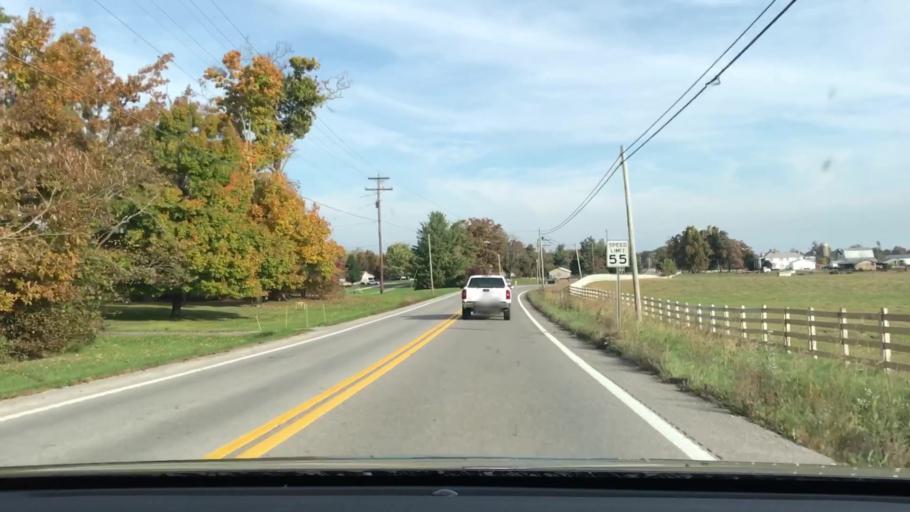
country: US
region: Tennessee
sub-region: Fentress County
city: Grimsley
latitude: 36.1945
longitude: -85.0205
